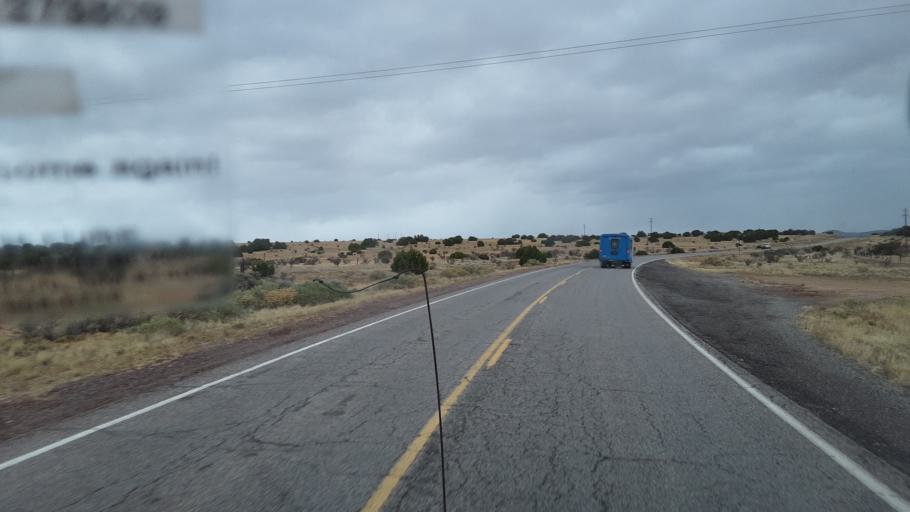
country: US
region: New Mexico
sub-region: Rio Arriba County
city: Santa Teresa
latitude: 36.2441
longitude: -106.4038
